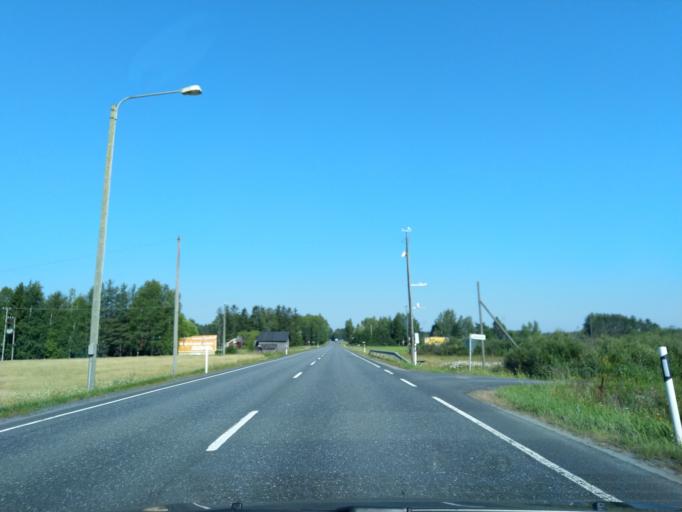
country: FI
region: Haeme
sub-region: Forssa
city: Humppila
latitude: 60.9557
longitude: 23.3346
